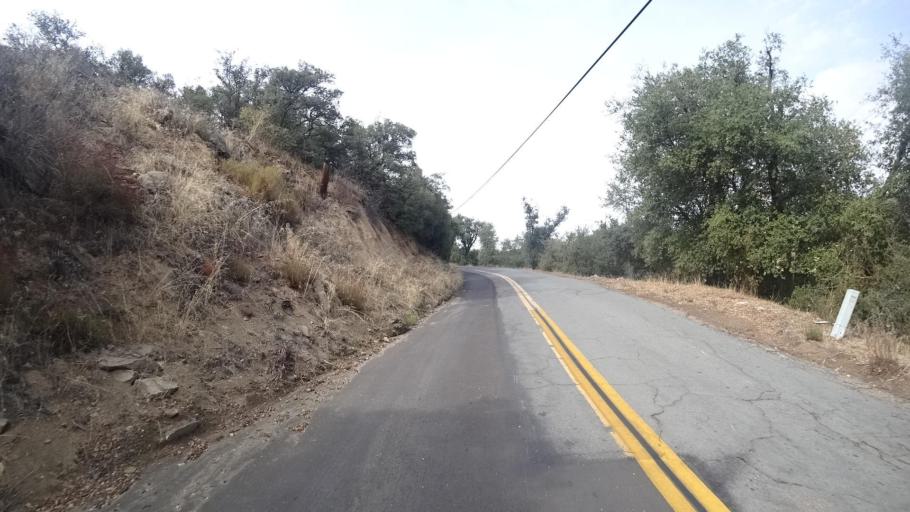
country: US
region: California
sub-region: San Diego County
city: Descanso
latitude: 32.8644
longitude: -116.6265
